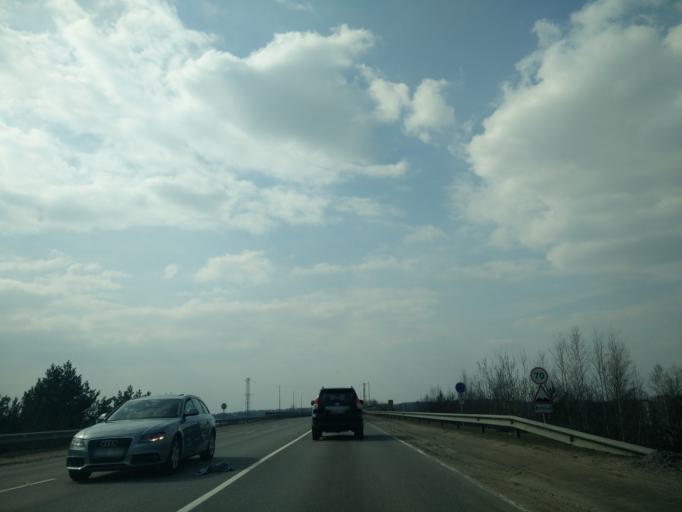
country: LT
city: Baltoji Voke
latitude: 54.6320
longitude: 25.1476
